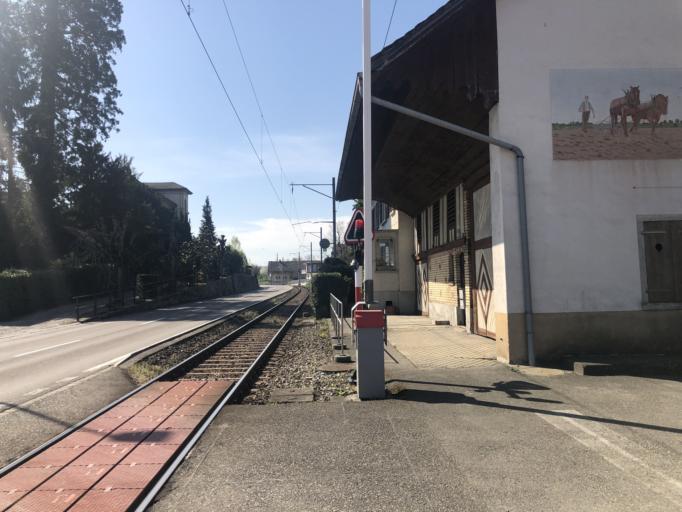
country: CH
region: Aargau
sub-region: Bezirk Kulm
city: Reinach
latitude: 47.2850
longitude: 8.1995
